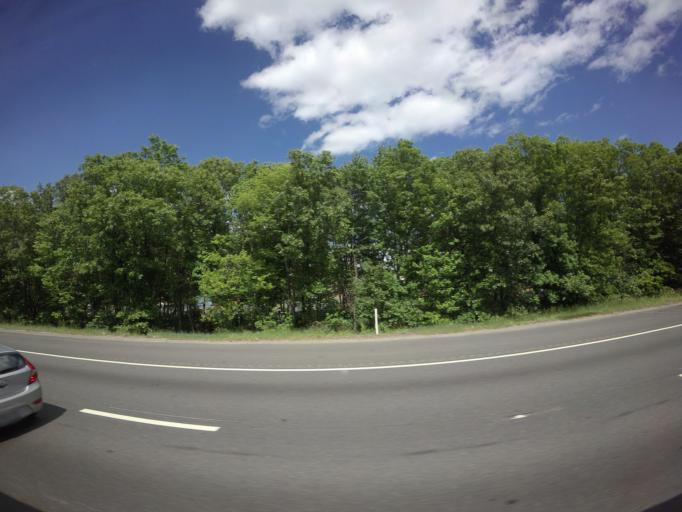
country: US
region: Massachusetts
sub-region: Middlesex County
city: Wilmington
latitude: 42.5619
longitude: -71.1424
